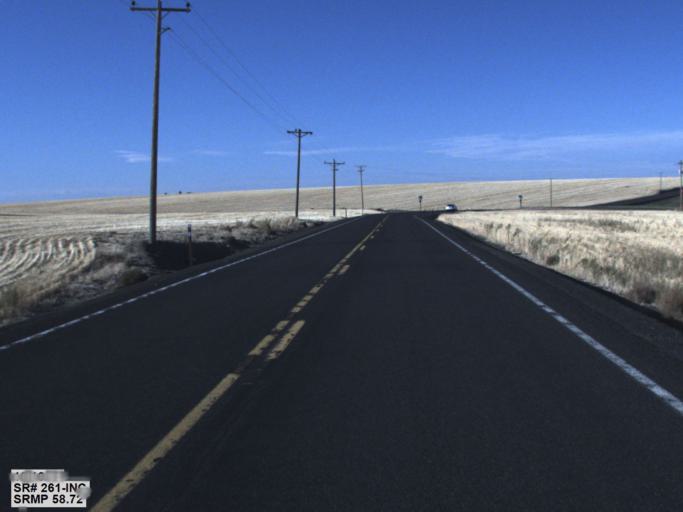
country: US
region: Washington
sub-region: Adams County
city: Ritzville
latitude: 47.0579
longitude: -118.3635
